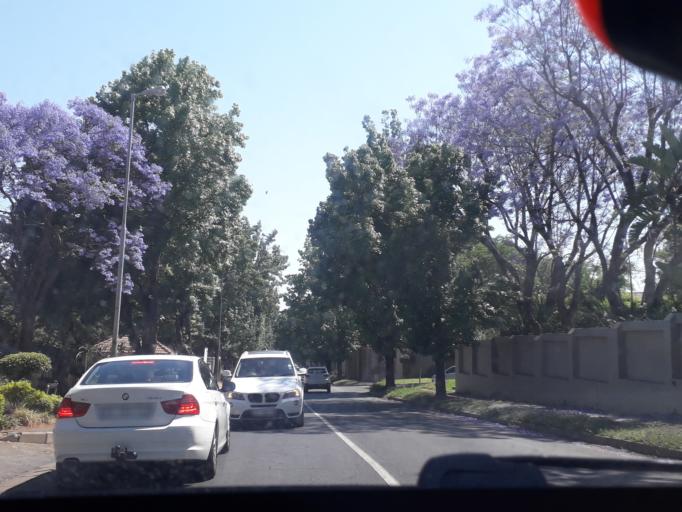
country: ZA
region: Gauteng
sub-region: City of Johannesburg Metropolitan Municipality
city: Johannesburg
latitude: -26.1343
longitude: 28.0714
